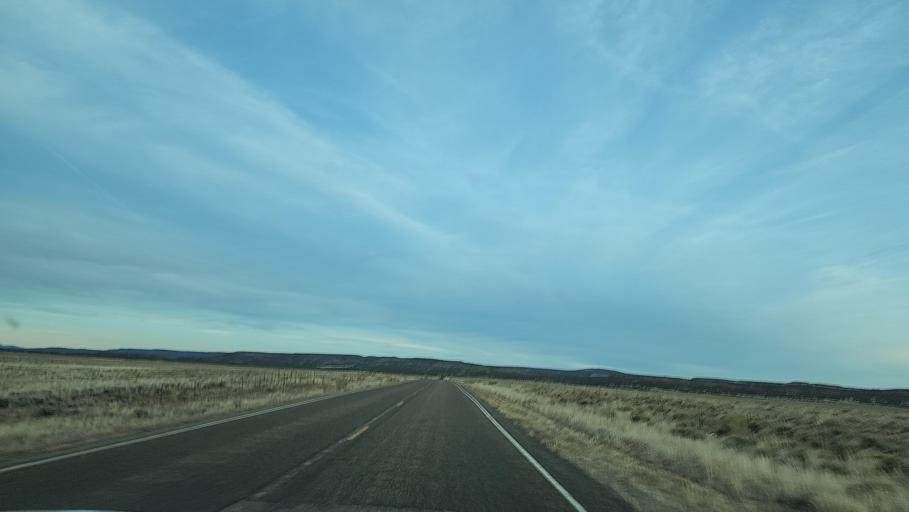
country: US
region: New Mexico
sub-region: Cibola County
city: Grants
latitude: 34.7046
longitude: -108.0216
